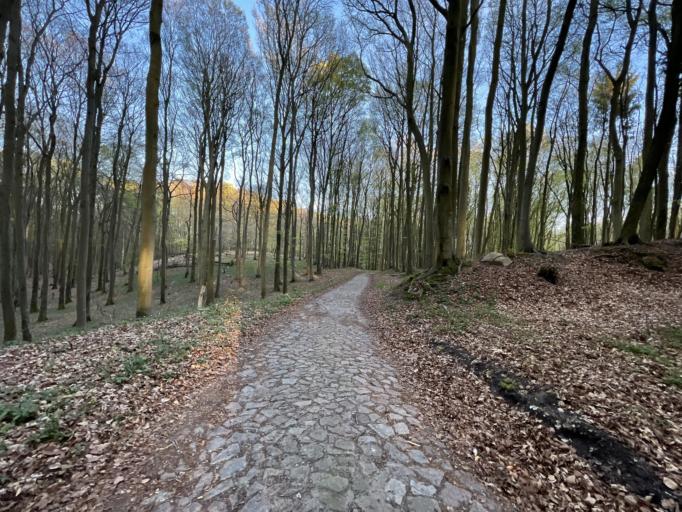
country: DE
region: Mecklenburg-Vorpommern
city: Sassnitz
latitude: 54.5307
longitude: 13.6544
